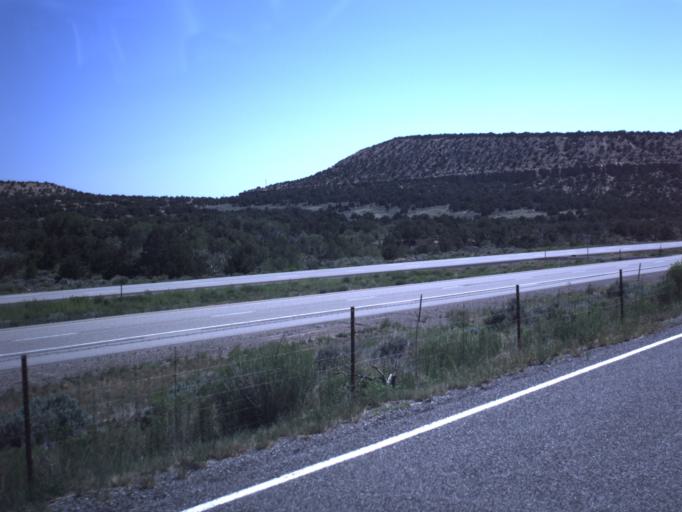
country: US
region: Utah
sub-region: Wayne County
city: Loa
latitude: 38.7573
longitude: -111.4128
